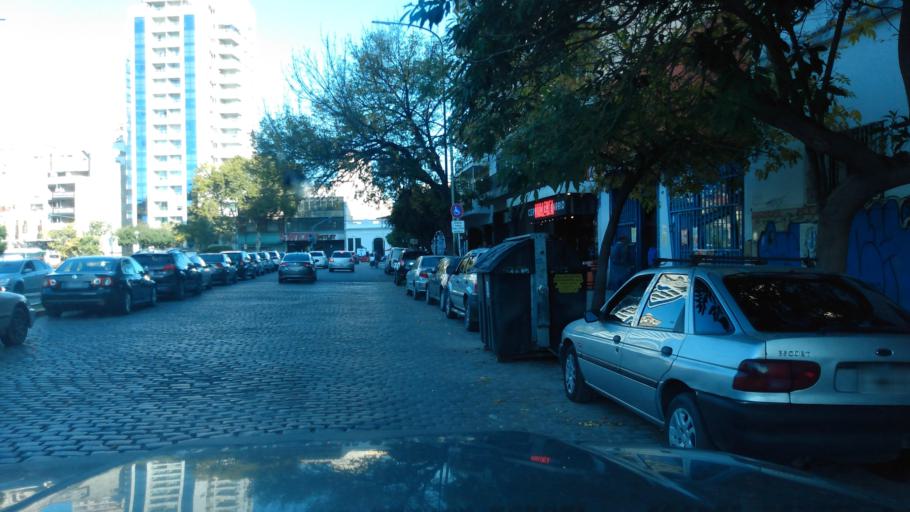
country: AR
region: Buenos Aires F.D.
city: Colegiales
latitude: -34.6080
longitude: -58.4377
